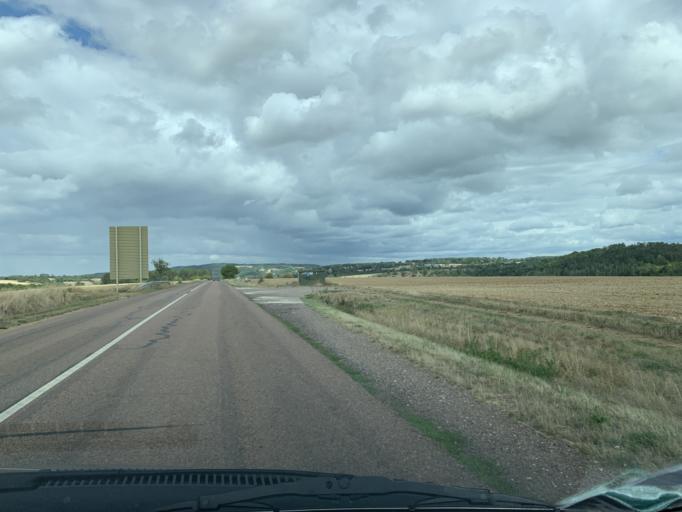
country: FR
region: Bourgogne
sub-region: Departement de la Nievre
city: Clamecy
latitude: 47.4403
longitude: 3.4918
